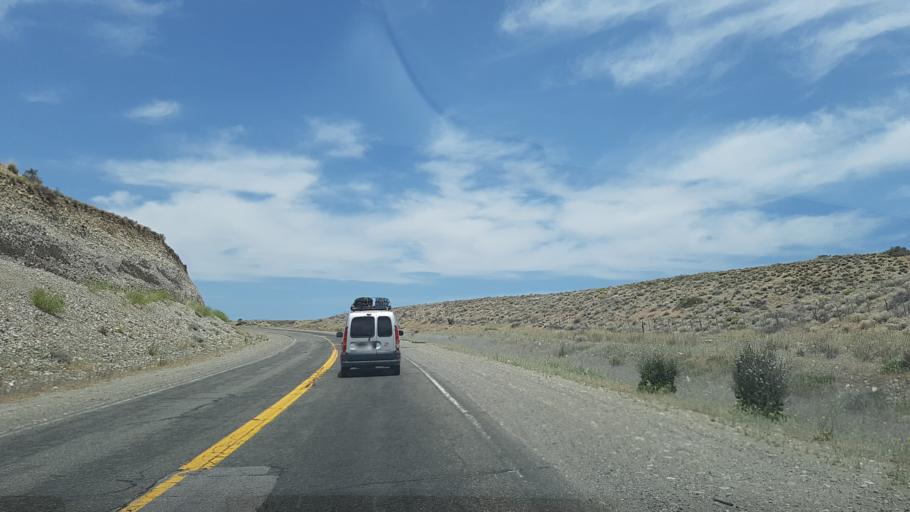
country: AR
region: Rio Negro
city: Pilcaniyeu
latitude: -40.4875
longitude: -70.6804
